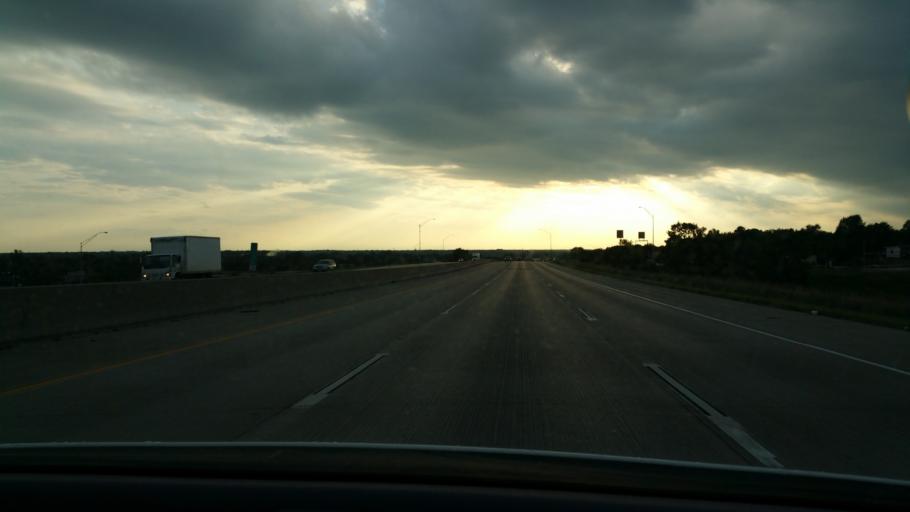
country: US
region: Iowa
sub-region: Polk County
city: Saylorville
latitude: 41.6502
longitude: -93.5968
